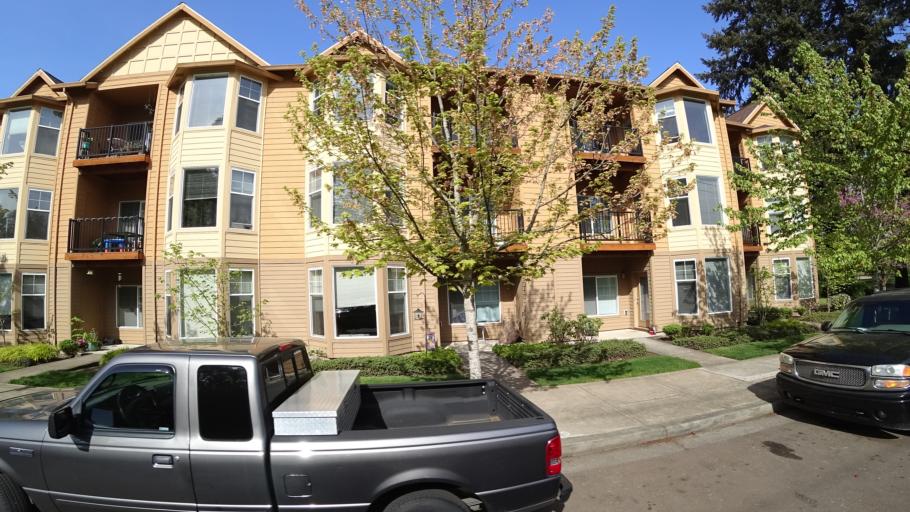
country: US
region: Oregon
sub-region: Washington County
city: Hillsboro
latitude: 45.5221
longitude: -122.9565
